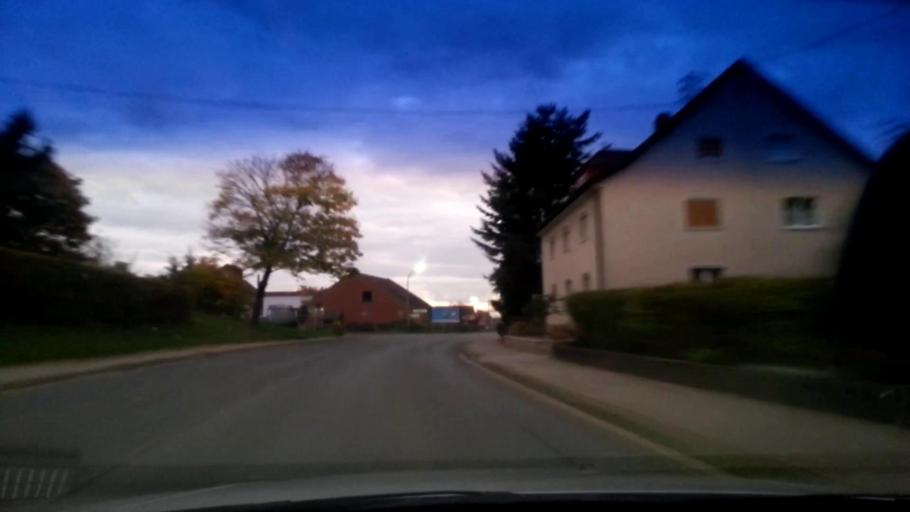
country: DE
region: Bavaria
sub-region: Upper Franconia
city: Schesslitz
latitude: 49.9736
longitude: 11.0290
